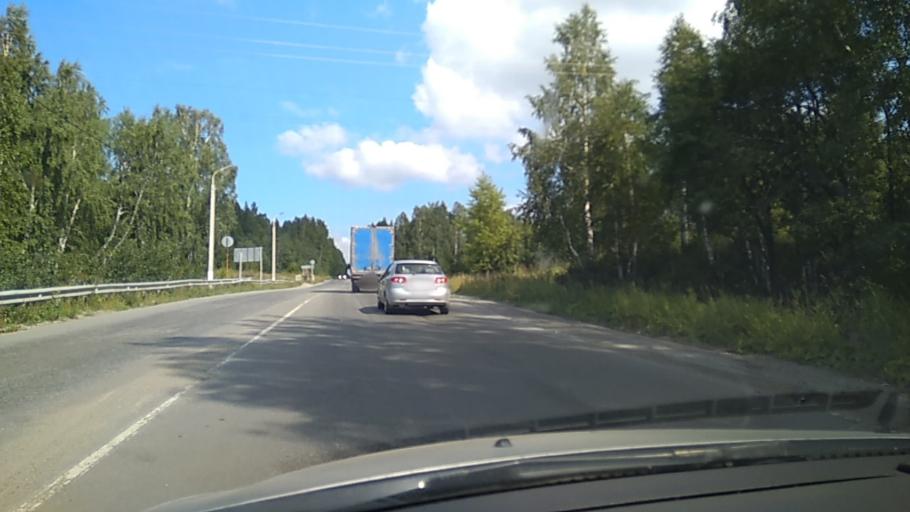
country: RU
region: Chelyabinsk
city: Zlatoust
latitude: 55.1177
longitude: 59.7457
